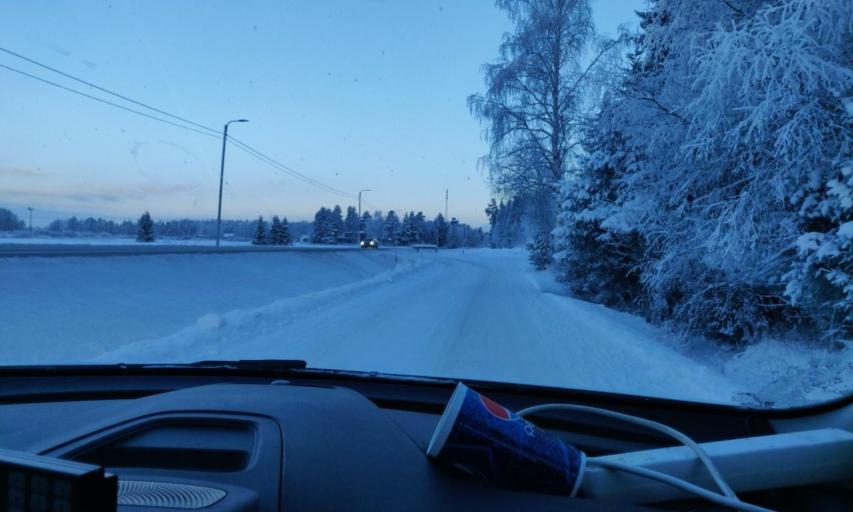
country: FI
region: Northern Ostrobothnia
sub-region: Ylivieska
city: Ylivieska
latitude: 64.0640
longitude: 24.4946
